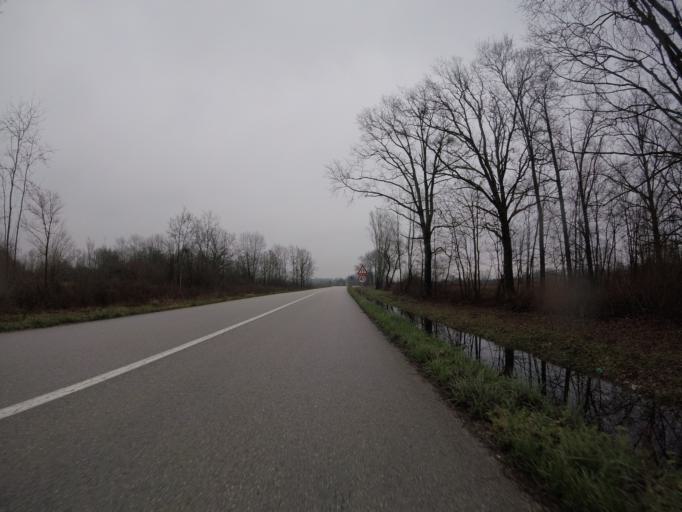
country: HR
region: Zagrebacka
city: Kuce
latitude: 45.7041
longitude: 16.1980
